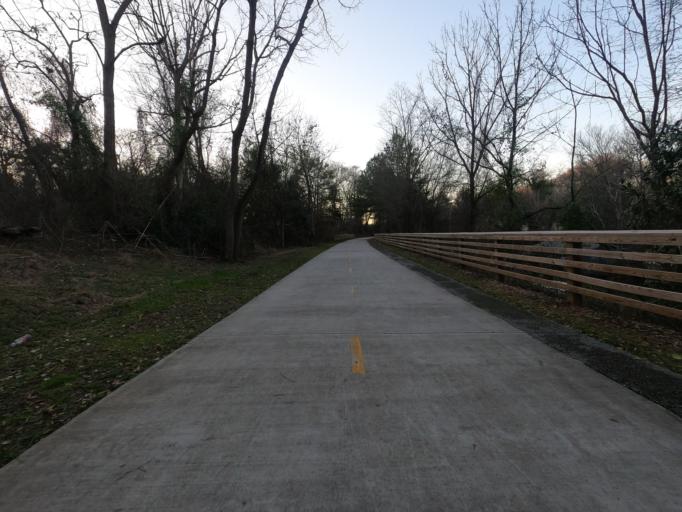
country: US
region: Georgia
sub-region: Clarke County
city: Athens
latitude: 33.9490
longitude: -83.3590
